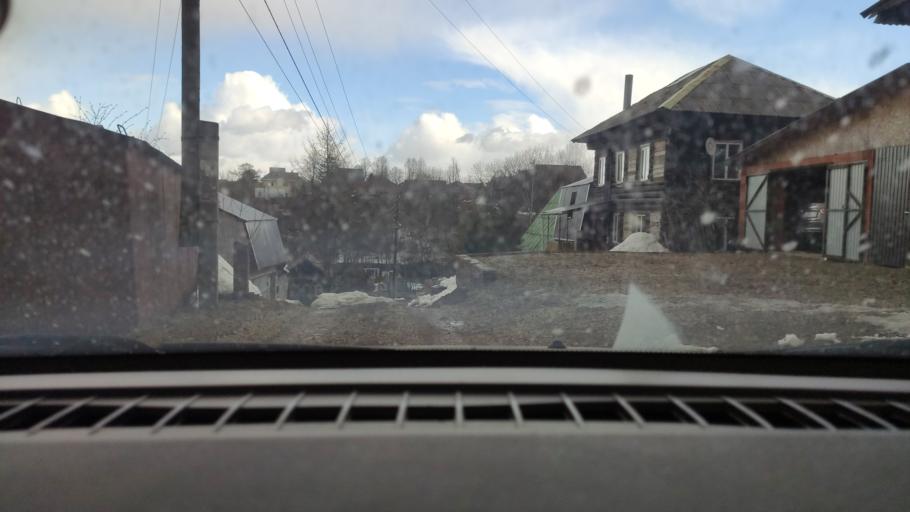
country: RU
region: Perm
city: Perm
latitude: 58.0393
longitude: 56.3321
